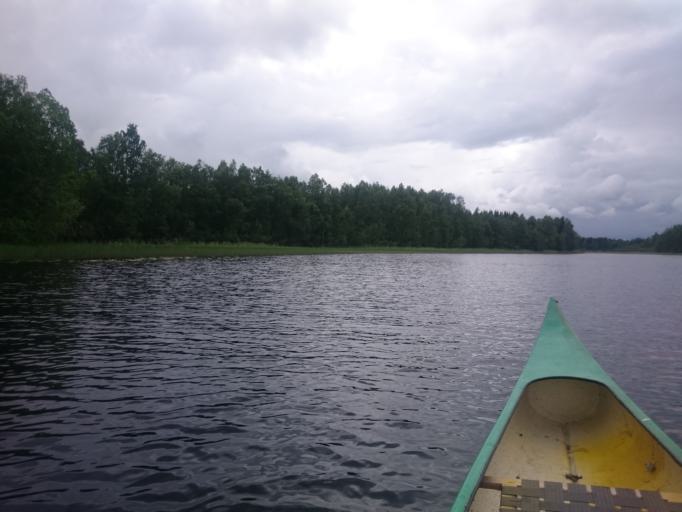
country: SE
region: Vaesternorrland
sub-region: OErnskoeldsviks Kommun
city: Ornskoldsvik
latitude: 63.6480
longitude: 18.6168
